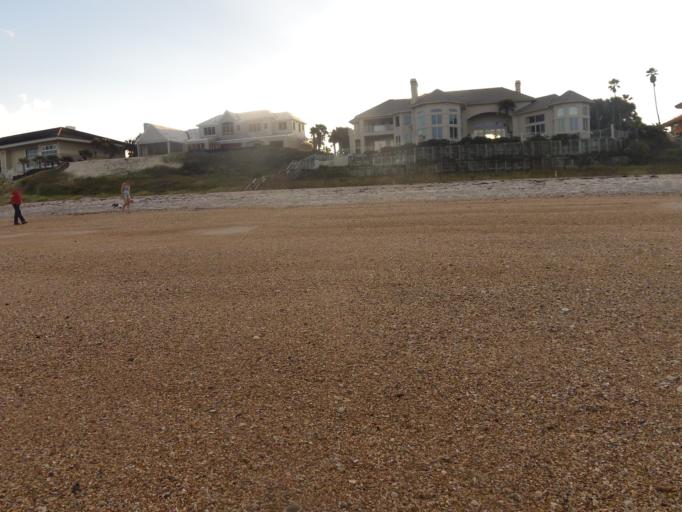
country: US
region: Florida
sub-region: Saint Johns County
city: Sawgrass
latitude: 30.1680
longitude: -81.3570
